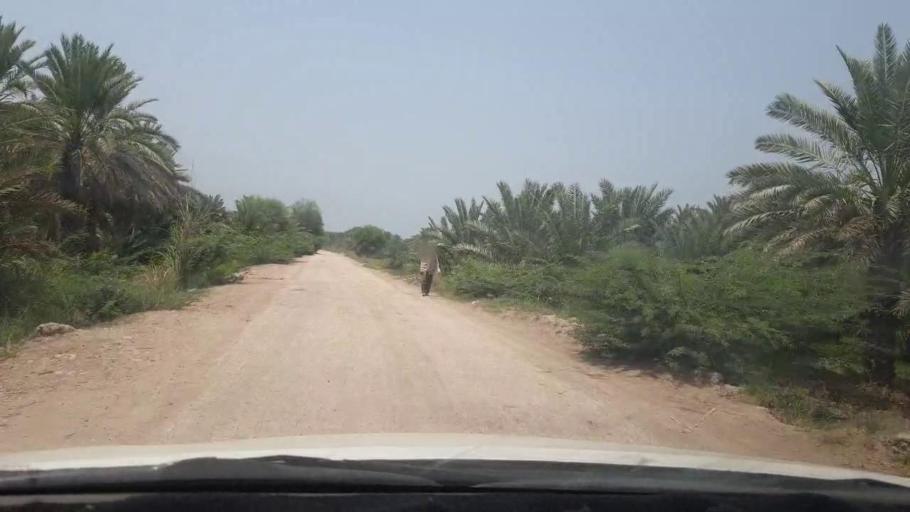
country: PK
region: Sindh
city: Khairpur
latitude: 27.4997
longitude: 68.8768
